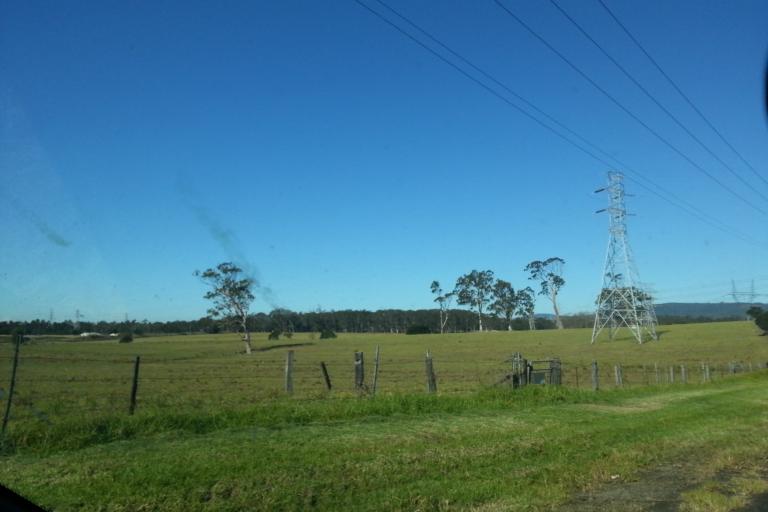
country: AU
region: New South Wales
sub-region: Wollongong
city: Dapto
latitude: -34.5209
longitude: 150.7794
